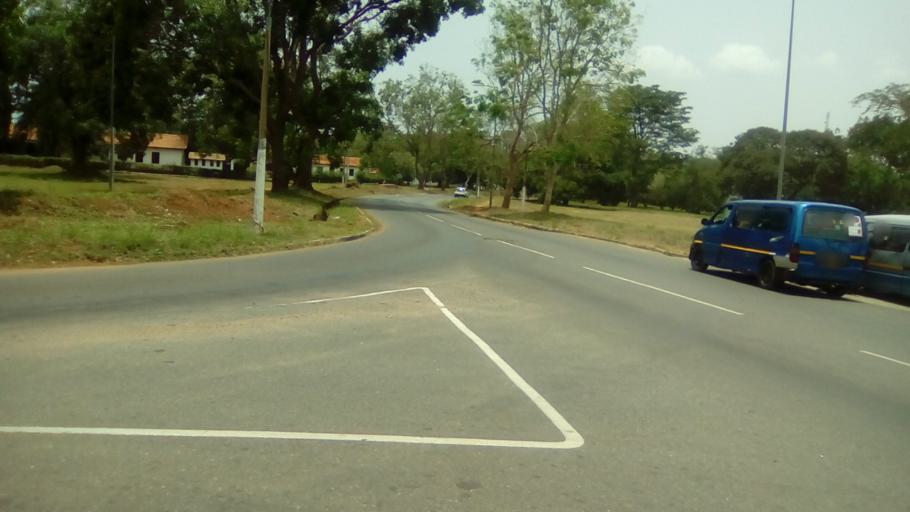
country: GH
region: Greater Accra
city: Medina Estates
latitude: 5.6436
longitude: -0.1892
